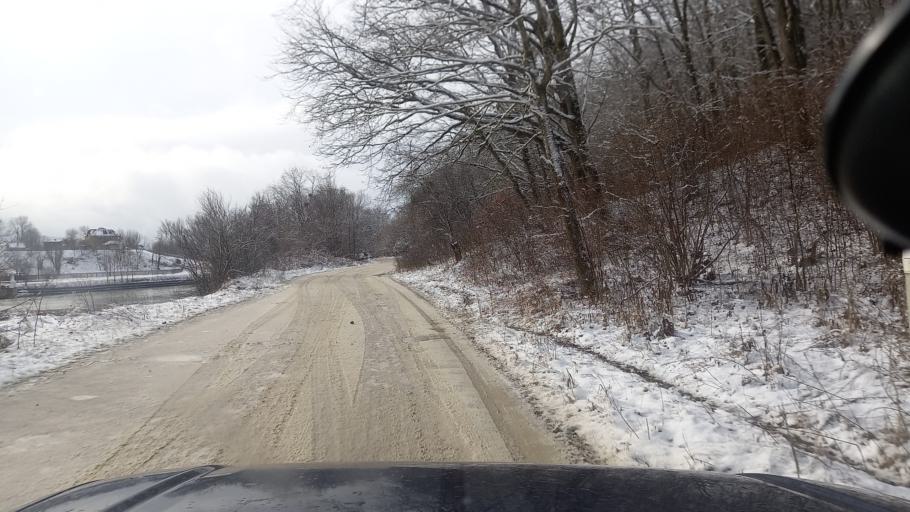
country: RU
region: Adygeya
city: Kamennomostskiy
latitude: 44.2410
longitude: 40.1969
